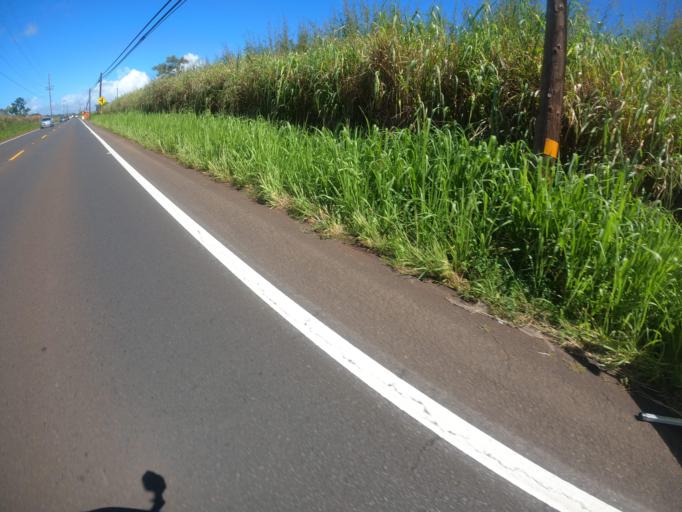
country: US
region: Hawaii
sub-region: Honolulu County
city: Schofield Barracks
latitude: 21.4681
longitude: -158.0539
